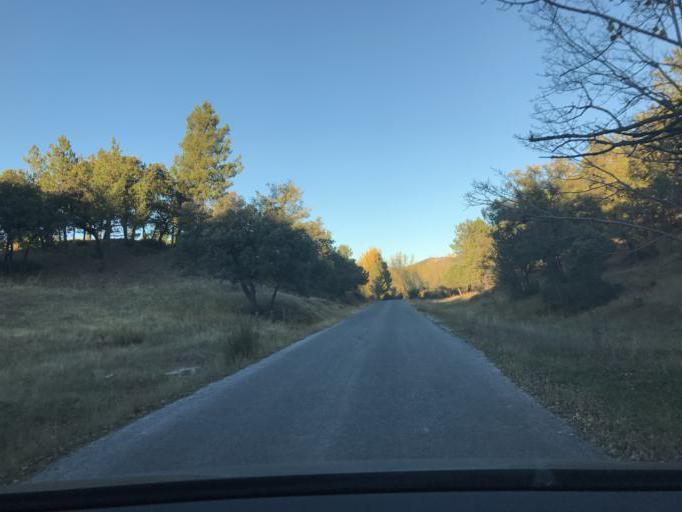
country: ES
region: Andalusia
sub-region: Provincia de Granada
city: Beas de Granada
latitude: 37.3031
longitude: -3.4680
